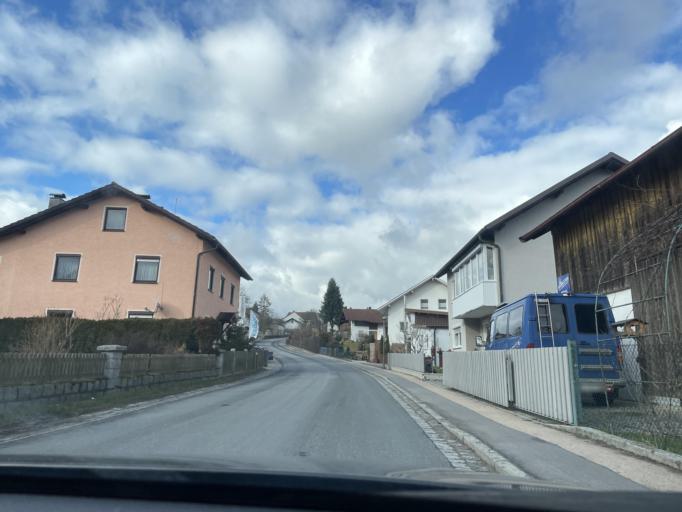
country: DE
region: Bavaria
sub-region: Upper Palatinate
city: Runding
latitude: 49.2133
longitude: 12.7671
